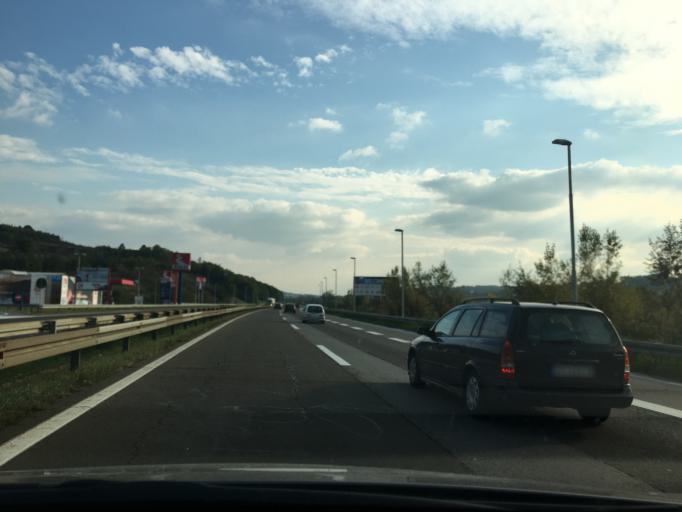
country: RS
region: Central Serbia
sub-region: Belgrade
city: Zvezdara
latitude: 44.6924
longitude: 20.5840
